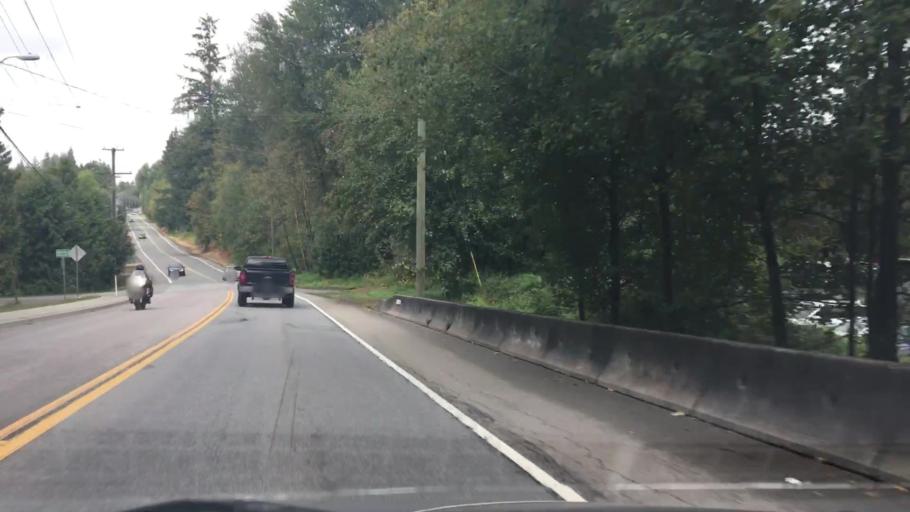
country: CA
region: British Columbia
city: Langley
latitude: 49.1040
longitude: -122.5715
